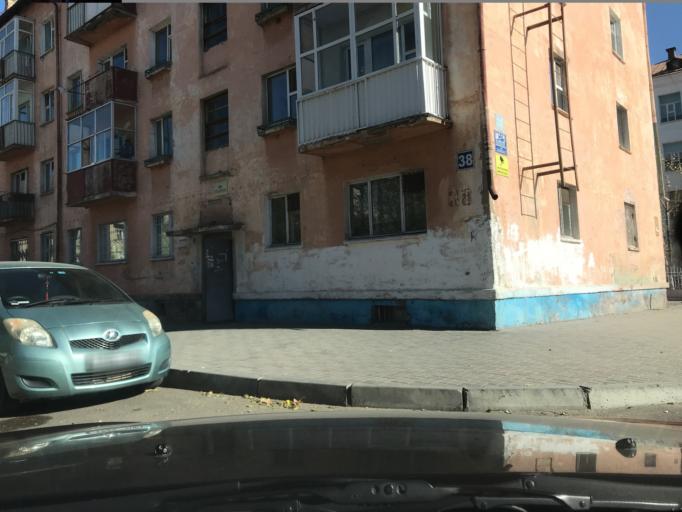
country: MN
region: Ulaanbaatar
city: Ulaanbaatar
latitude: 47.9188
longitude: 106.9080
